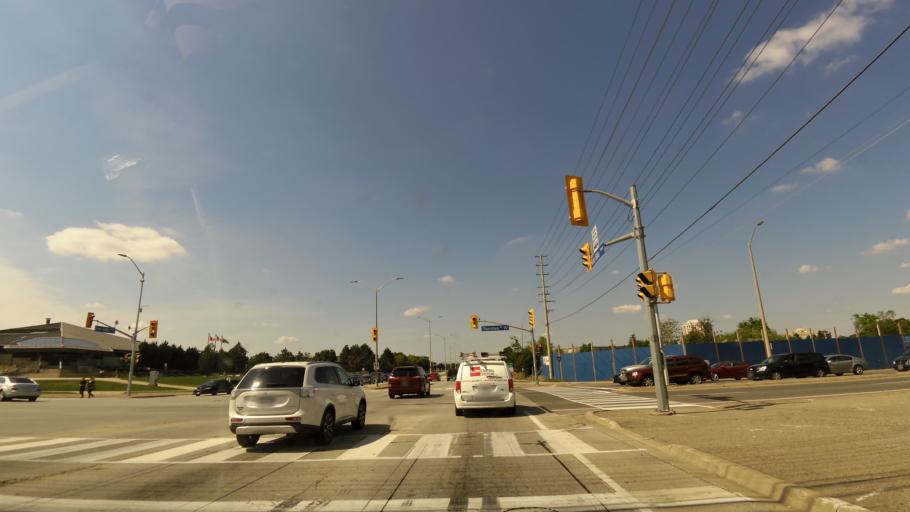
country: CA
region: Ontario
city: Mississauga
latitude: 43.5368
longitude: -79.6659
